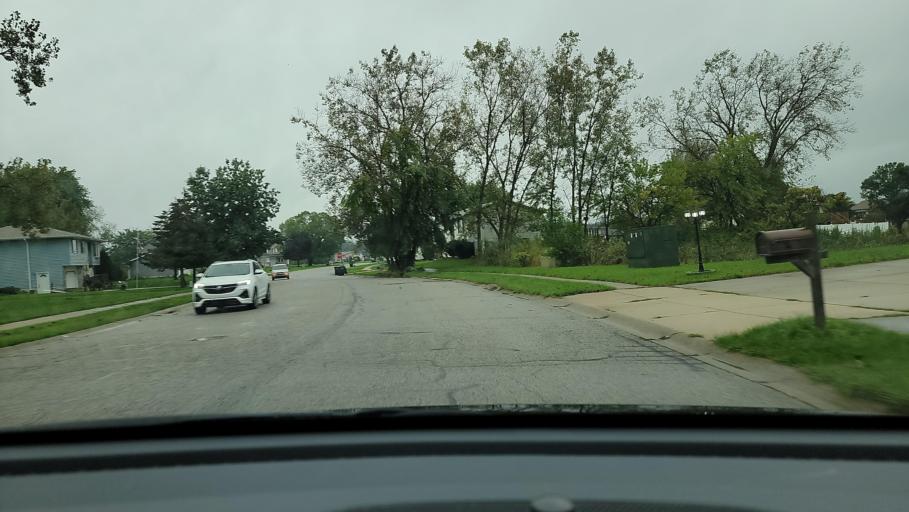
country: US
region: Indiana
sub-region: Porter County
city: Portage
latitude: 41.5638
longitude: -87.1703
